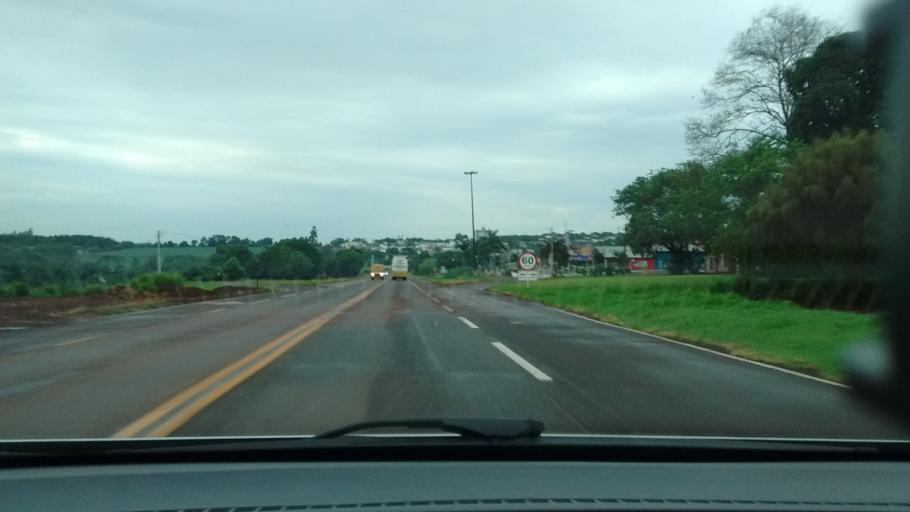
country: BR
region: Parana
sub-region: Corbelia
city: Corbelia
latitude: -24.7794
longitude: -53.2919
